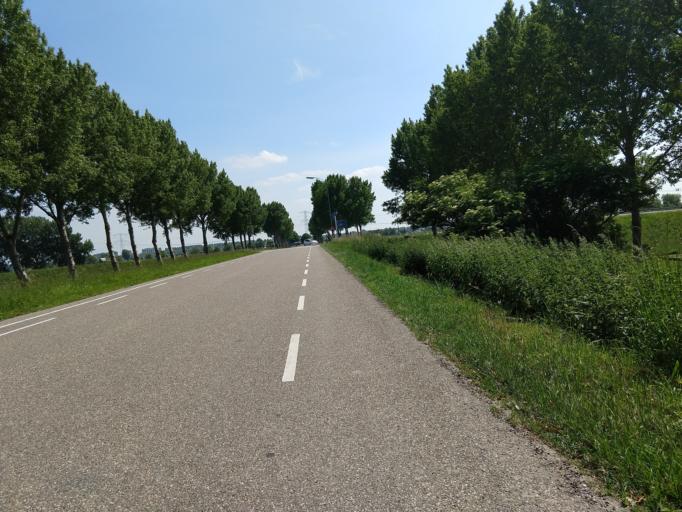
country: NL
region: Zeeland
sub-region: Gemeente Borsele
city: Borssele
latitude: 51.4424
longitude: 3.7686
